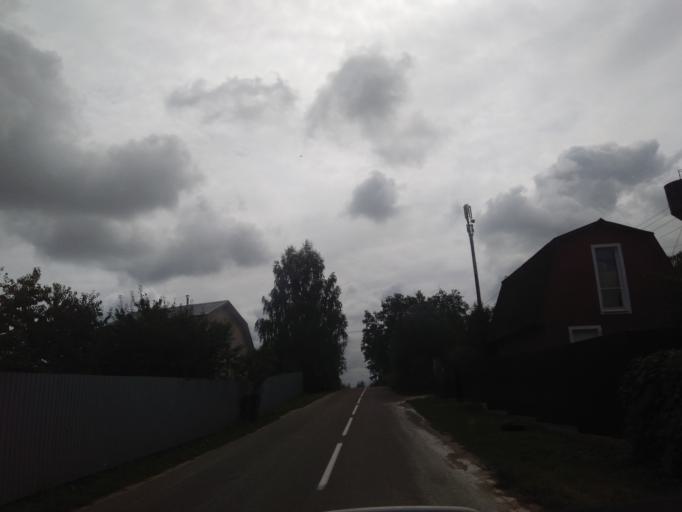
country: BY
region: Minsk
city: Slabada
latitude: 53.9828
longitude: 27.9034
